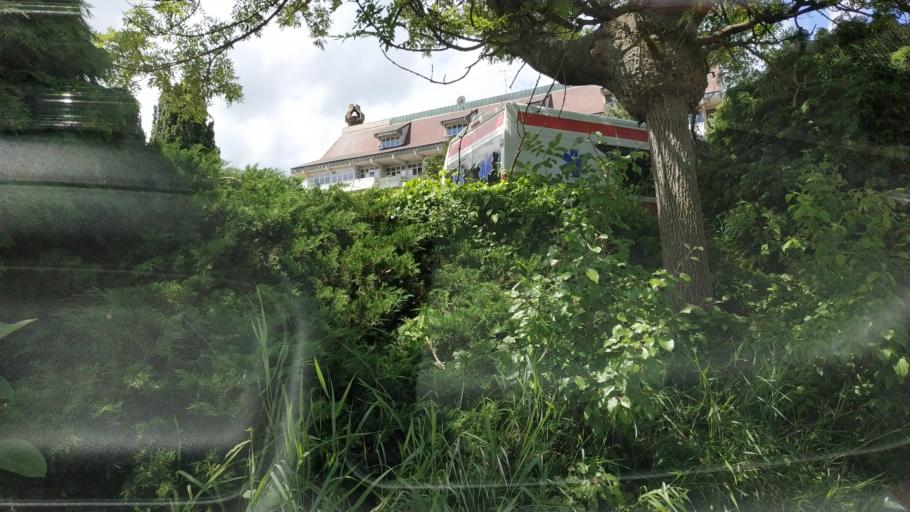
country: RS
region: Central Serbia
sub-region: Zajecarski Okrug
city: Soko Banja
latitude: 43.6390
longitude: 21.8694
